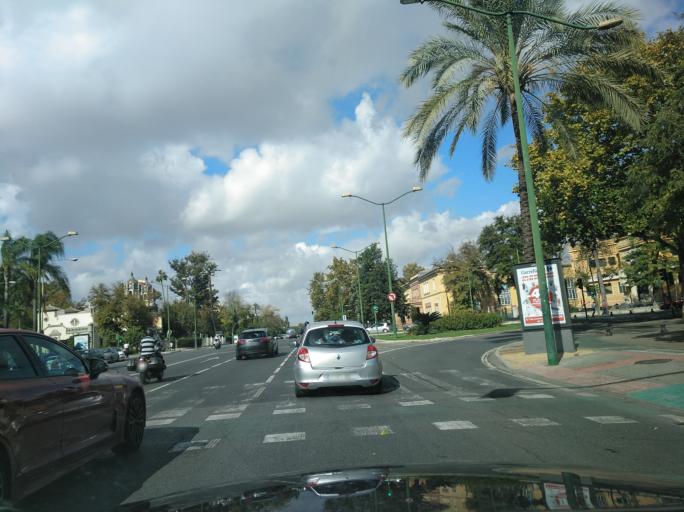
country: ES
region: Andalusia
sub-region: Provincia de Sevilla
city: Sevilla
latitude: 37.3688
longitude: -5.9875
